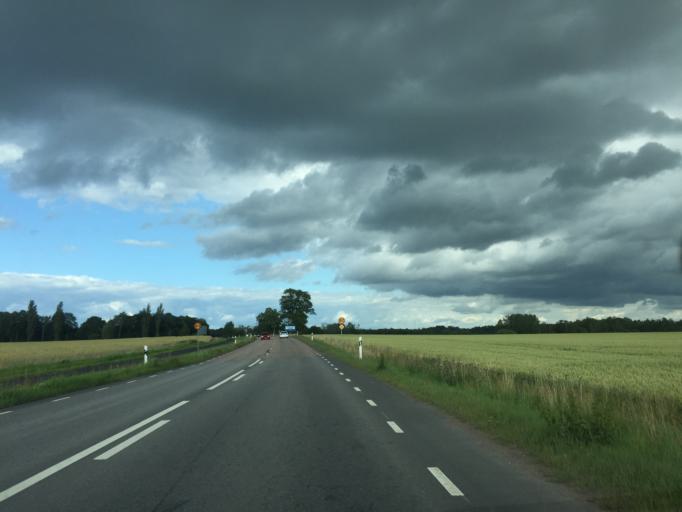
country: SE
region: OEstergoetland
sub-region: Vadstena Kommun
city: Vadstena
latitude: 58.4581
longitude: 14.9233
